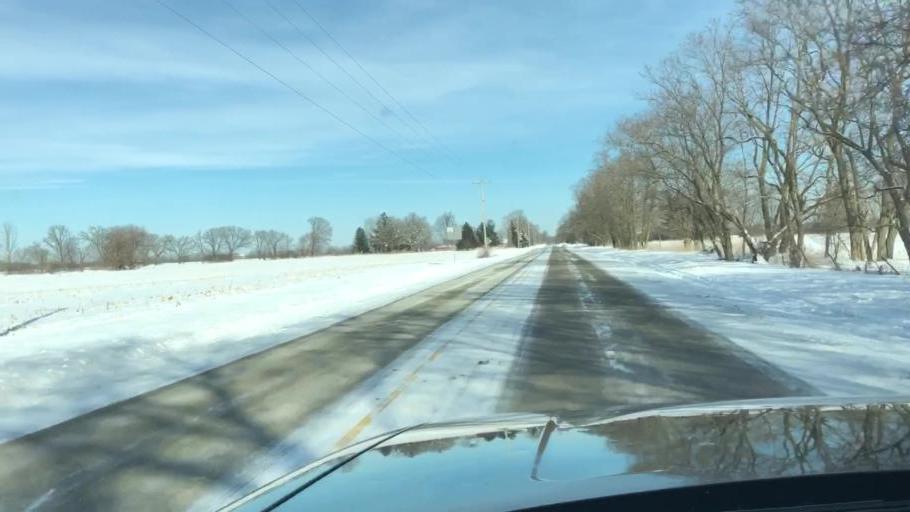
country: US
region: Wisconsin
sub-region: Jefferson County
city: Palmyra
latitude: 42.9058
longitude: -88.5408
